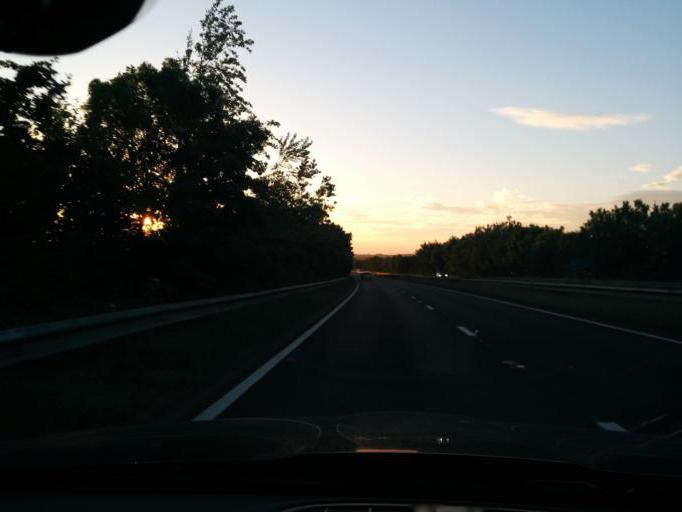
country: GB
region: England
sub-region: Northumberland
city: Seghill
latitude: 55.0501
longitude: -1.5543
